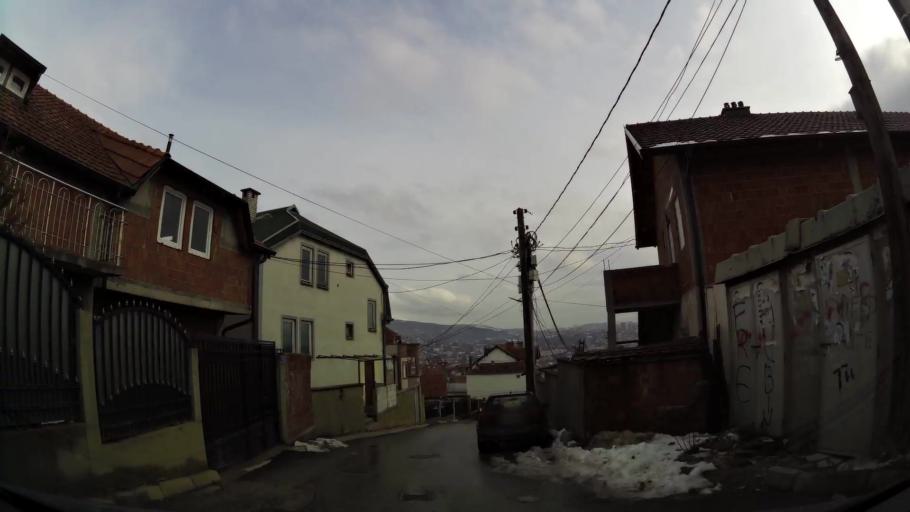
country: XK
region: Pristina
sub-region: Komuna e Prishtines
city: Pristina
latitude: 42.6744
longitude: 21.1585
